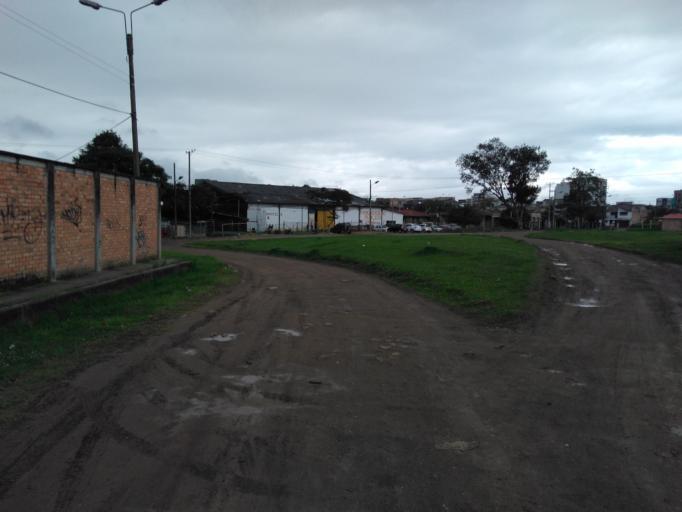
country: CO
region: Cauca
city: Popayan
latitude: 2.4536
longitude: -76.5917
